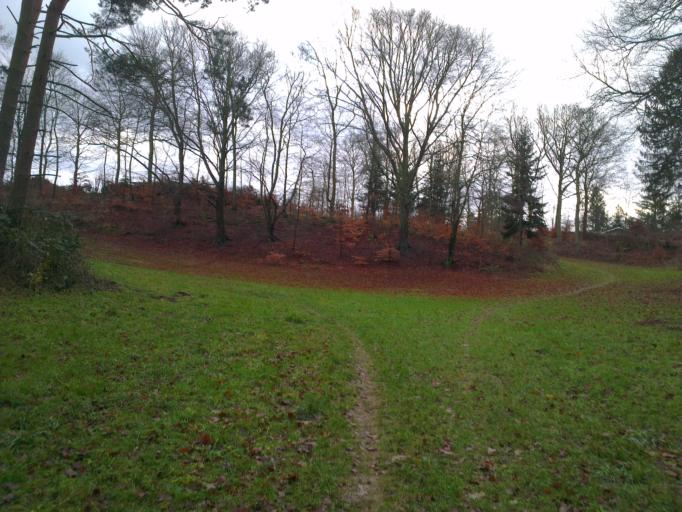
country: DK
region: Capital Region
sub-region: Frederikssund Kommune
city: Jaegerspris
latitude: 55.8517
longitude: 12.0061
